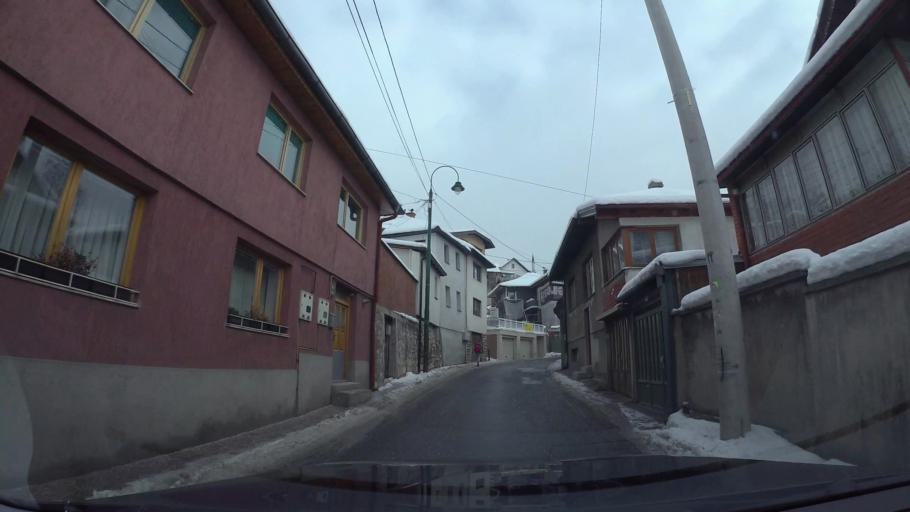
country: BA
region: Federation of Bosnia and Herzegovina
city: Kobilja Glava
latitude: 43.8635
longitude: 18.4387
